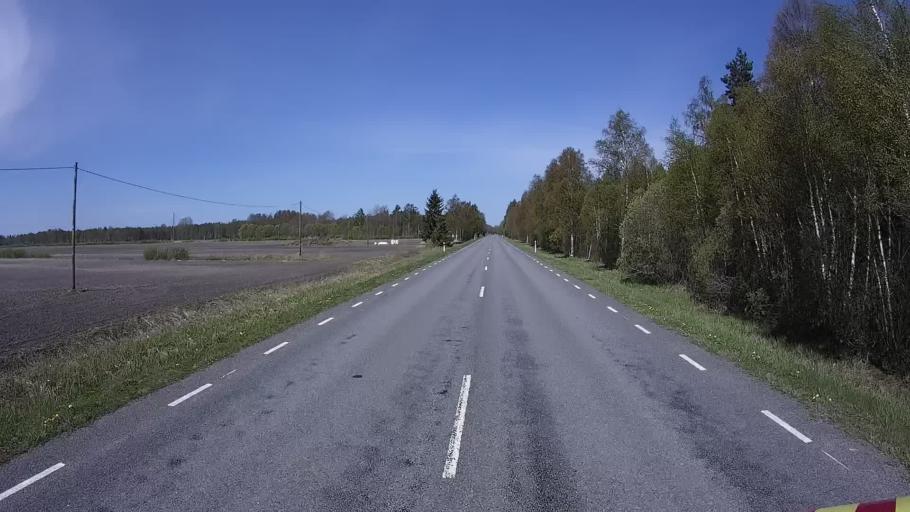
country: EE
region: Laeaene
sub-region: Lihula vald
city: Lihula
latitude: 58.6407
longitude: 23.8558
